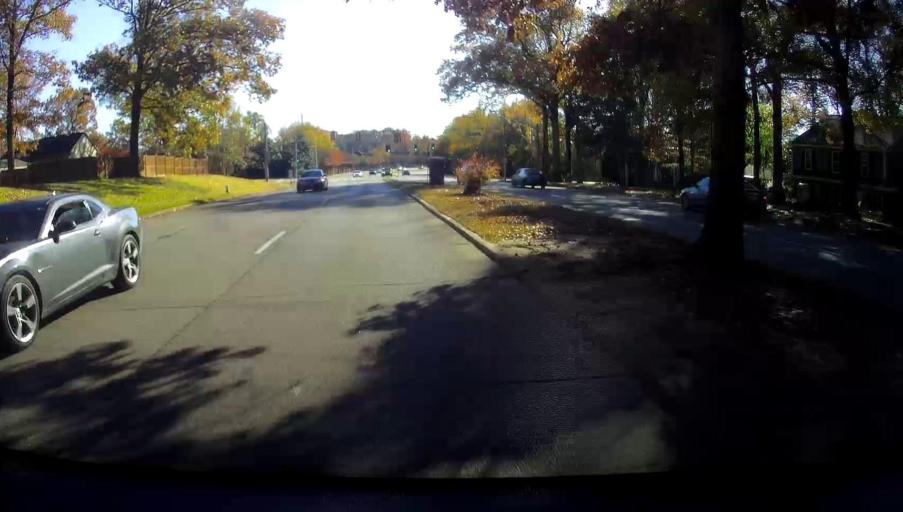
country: US
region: Tennessee
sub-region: Shelby County
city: Germantown
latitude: 35.0839
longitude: -89.8403
